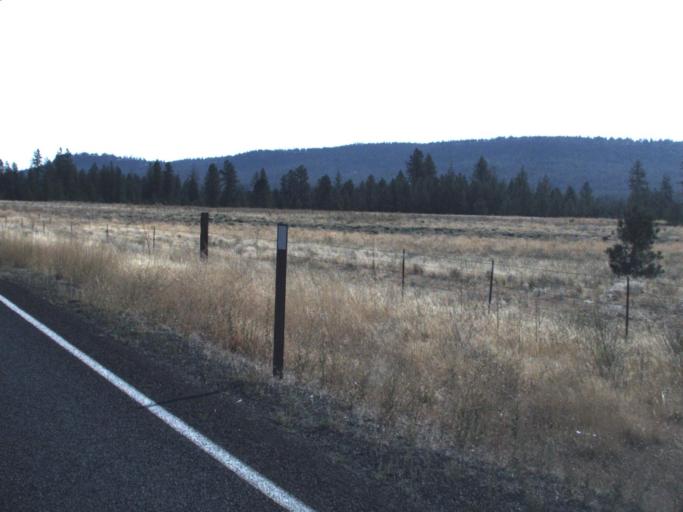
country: US
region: Washington
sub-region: Spokane County
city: Fairchild Air Force Base
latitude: 47.8385
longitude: -117.7531
